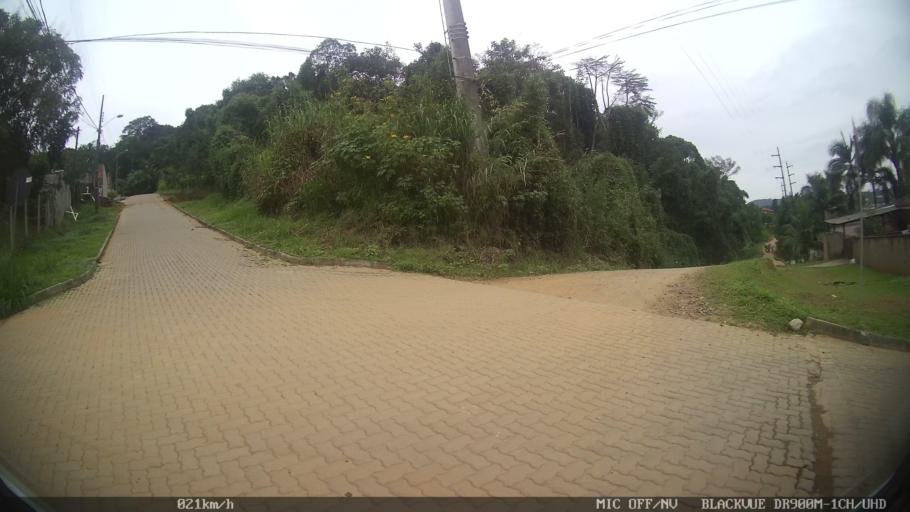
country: BR
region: Santa Catarina
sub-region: Joinville
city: Joinville
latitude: -26.3656
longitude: -48.8198
